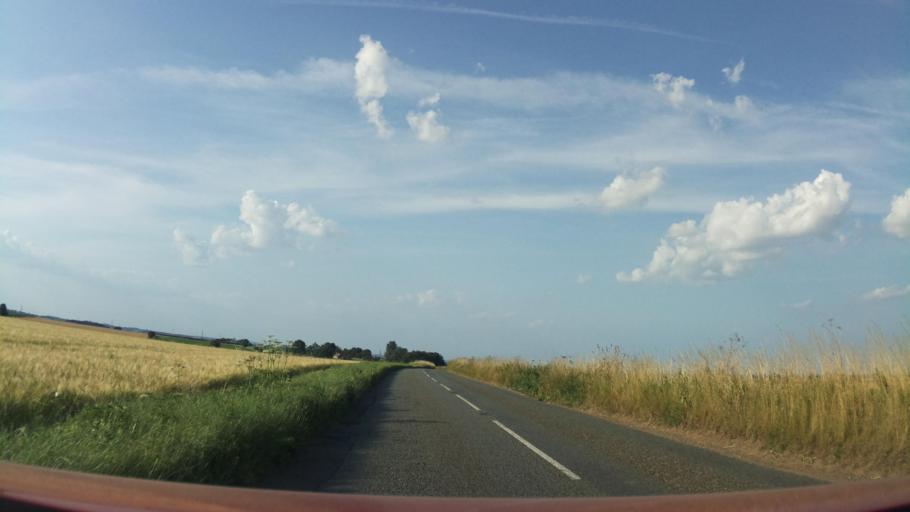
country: GB
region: England
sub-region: South Gloucestershire
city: Marshfield
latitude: 51.4713
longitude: -2.3120
